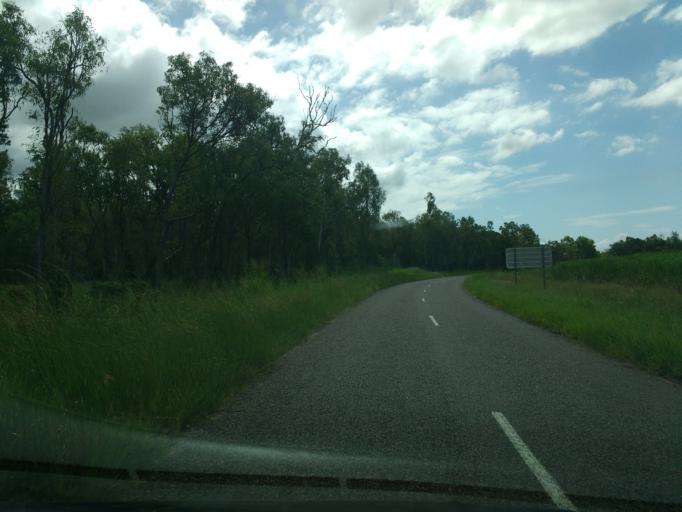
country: AU
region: Queensland
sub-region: Hinchinbrook
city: Ingham
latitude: -18.9898
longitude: 146.2952
